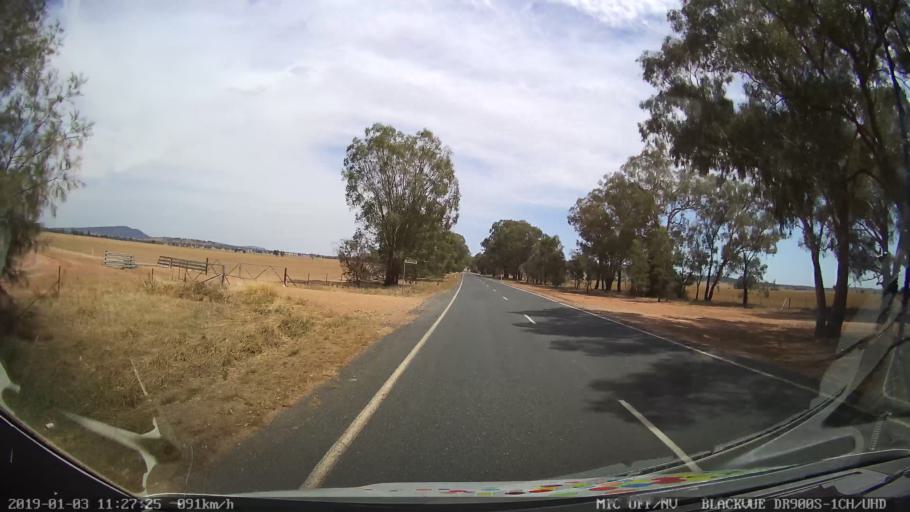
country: AU
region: New South Wales
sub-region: Weddin
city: Grenfell
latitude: -34.0128
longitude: 148.2192
